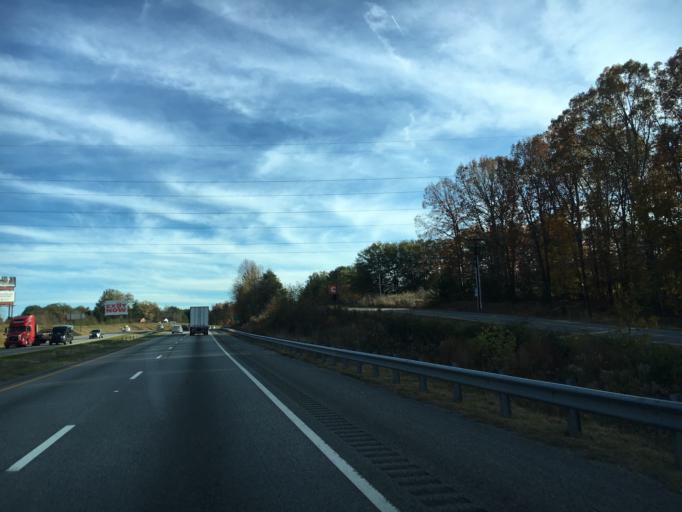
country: US
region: South Carolina
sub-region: Spartanburg County
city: Southern Shops
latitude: 35.0045
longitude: -82.0241
